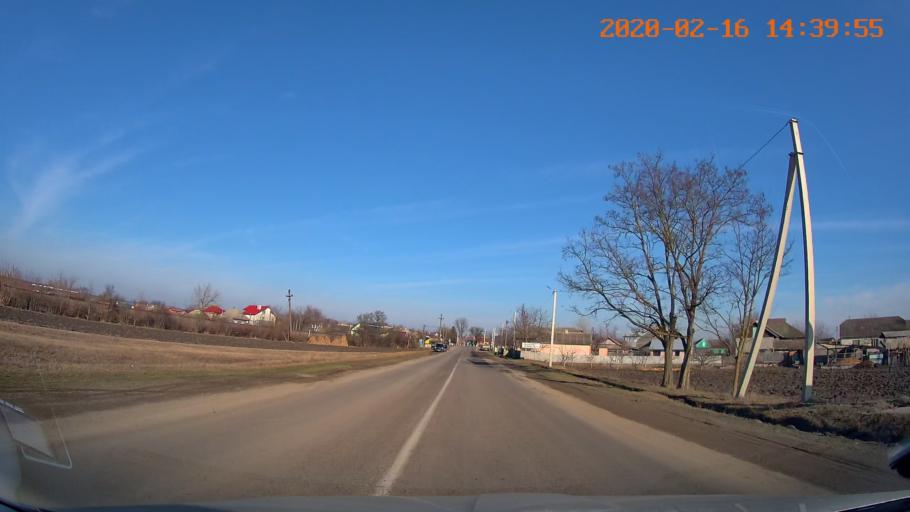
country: RO
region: Botosani
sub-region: Comuna Darabani
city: Bajura
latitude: 48.2473
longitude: 26.5547
